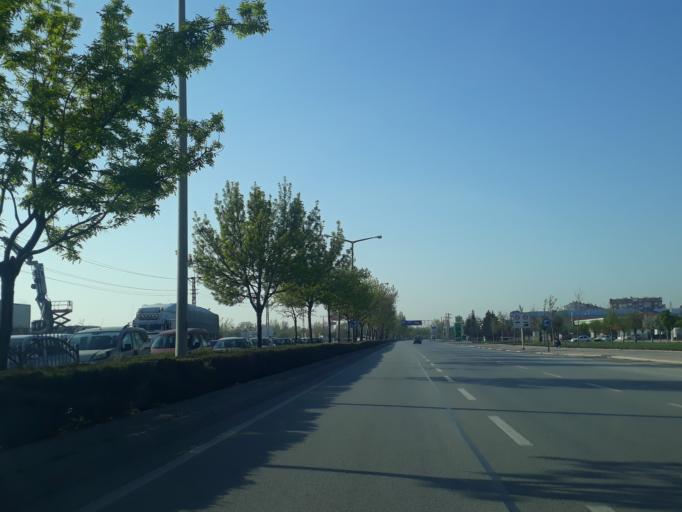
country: TR
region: Konya
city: Selcuklu
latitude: 37.8785
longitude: 32.5463
